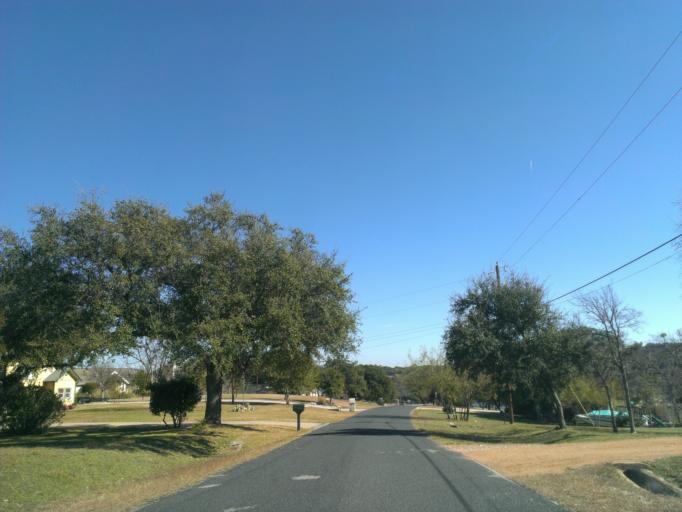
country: US
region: Texas
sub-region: Travis County
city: Briarcliff
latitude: 30.4322
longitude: -98.0644
